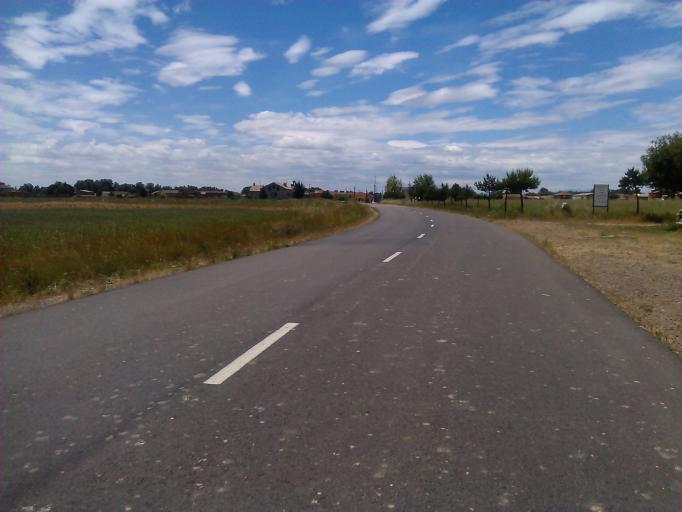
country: ES
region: Castille and Leon
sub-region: Provincia de Leon
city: Chozas de Abajo
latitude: 42.4864
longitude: -5.7221
